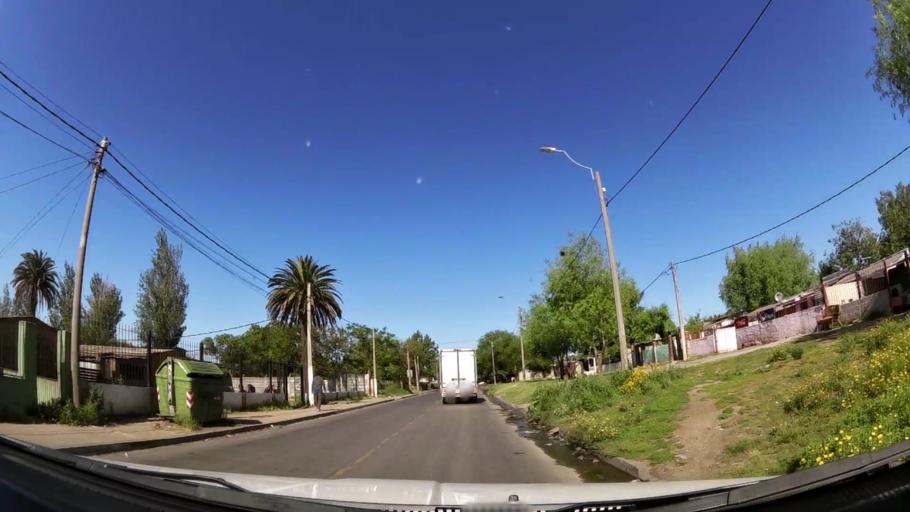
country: UY
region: Montevideo
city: Montevideo
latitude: -34.8345
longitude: -56.1580
